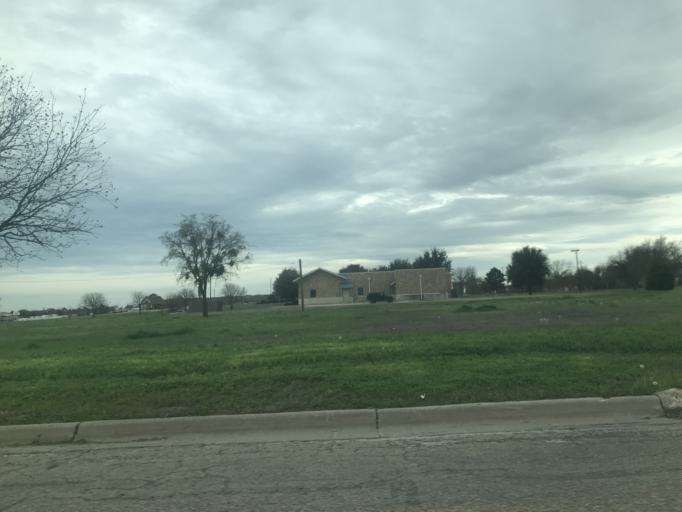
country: US
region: Texas
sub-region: Taylor County
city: Abilene
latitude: 32.4716
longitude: -99.7280
